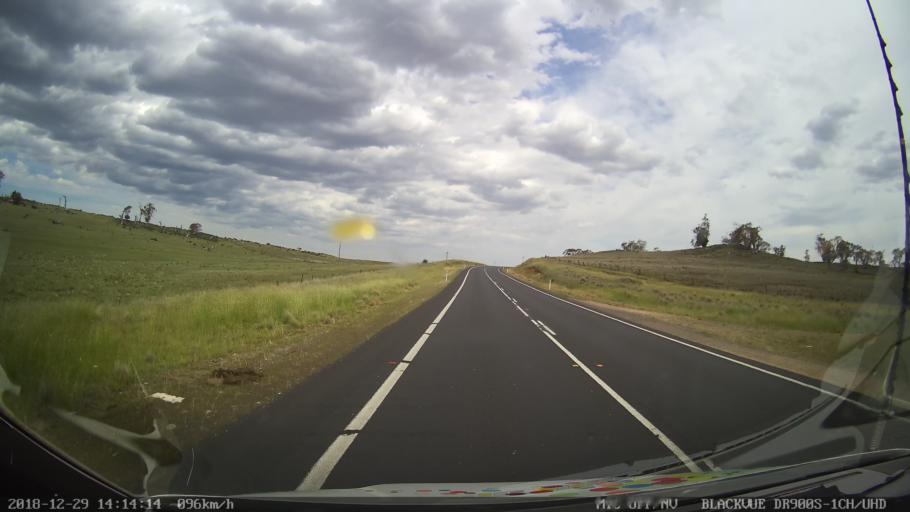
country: AU
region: New South Wales
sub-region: Cooma-Monaro
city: Cooma
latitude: -36.4396
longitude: 149.2374
